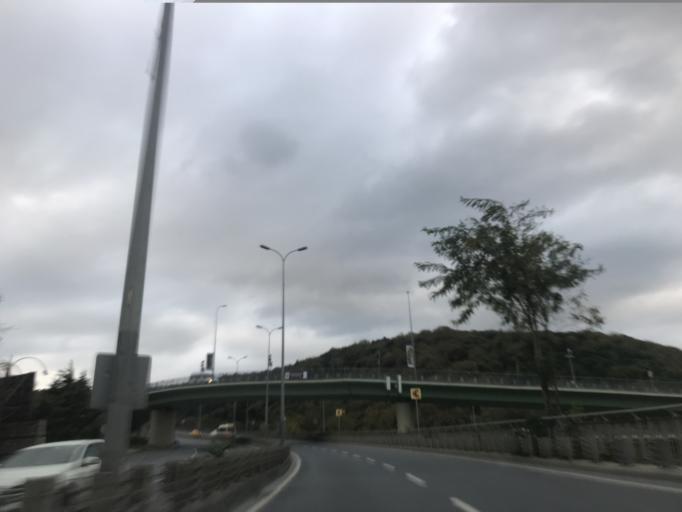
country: TR
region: Istanbul
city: Arikoey
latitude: 41.1525
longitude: 29.0318
